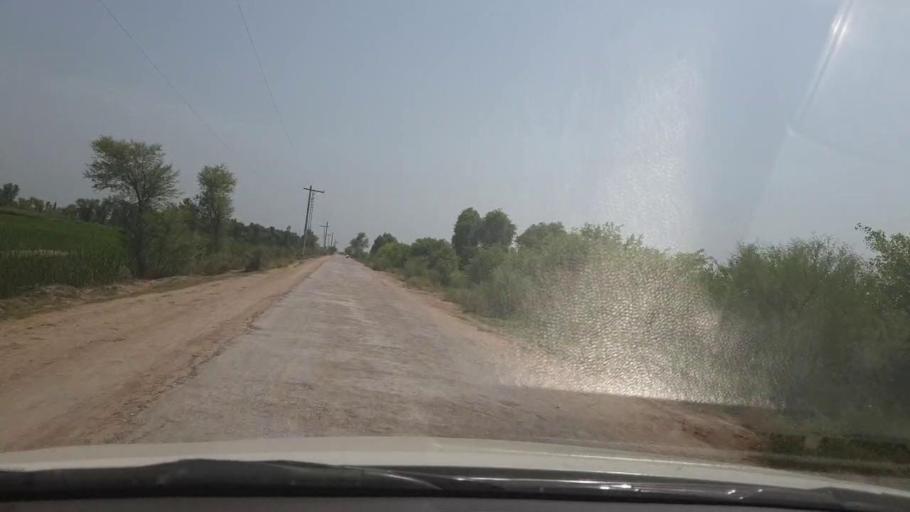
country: PK
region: Sindh
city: Garhi Yasin
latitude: 27.9722
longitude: 68.5035
